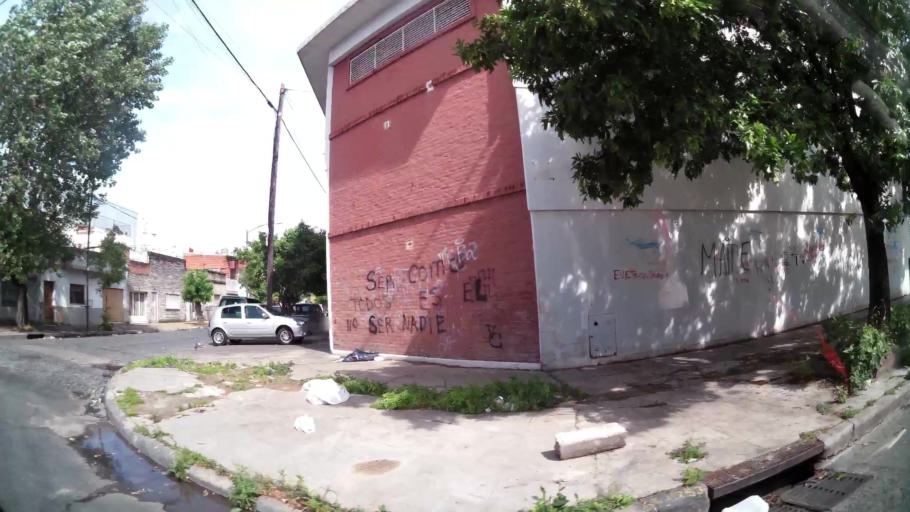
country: AR
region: Buenos Aires F.D.
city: Villa Lugano
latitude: -34.6524
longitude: -58.4309
